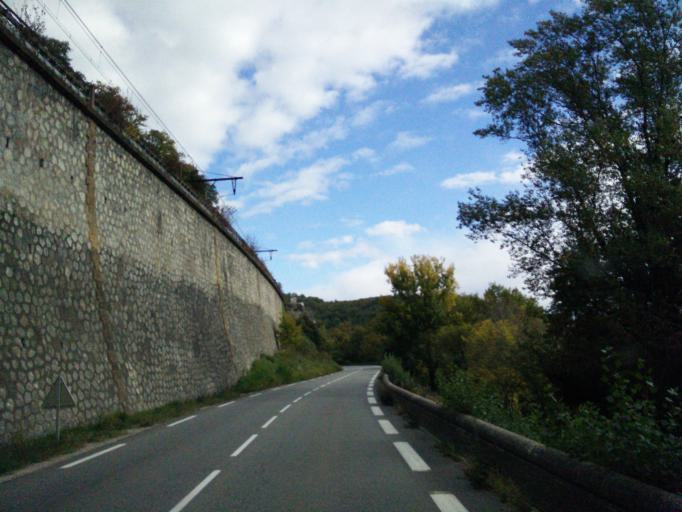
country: FR
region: Midi-Pyrenees
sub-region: Departement du Lot
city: Pradines
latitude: 44.4941
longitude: 1.4001
